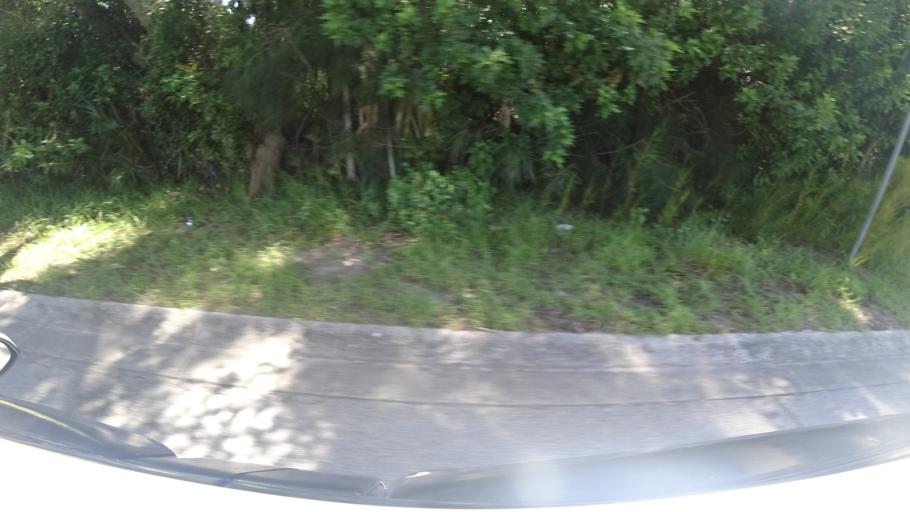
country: US
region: Florida
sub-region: Sarasota County
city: North Sarasota
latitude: 27.4041
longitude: -82.5308
